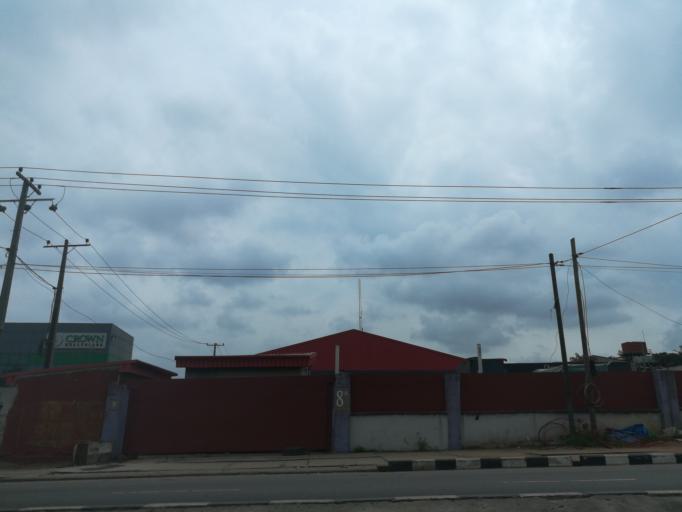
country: NG
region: Lagos
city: Ikeja
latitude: 6.6073
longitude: 3.3587
